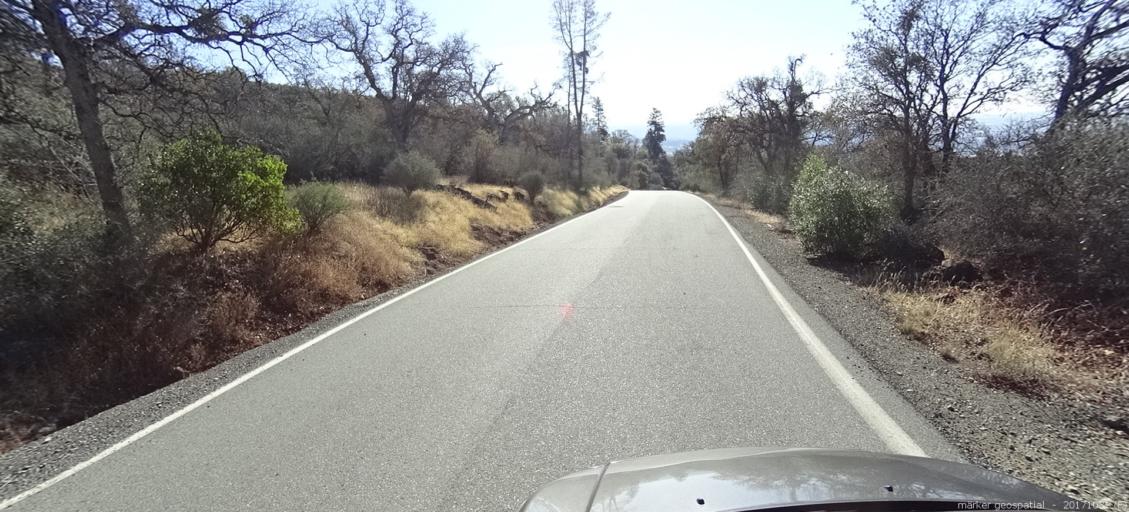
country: US
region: California
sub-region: Shasta County
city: Shingletown
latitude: 40.4667
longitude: -121.8827
